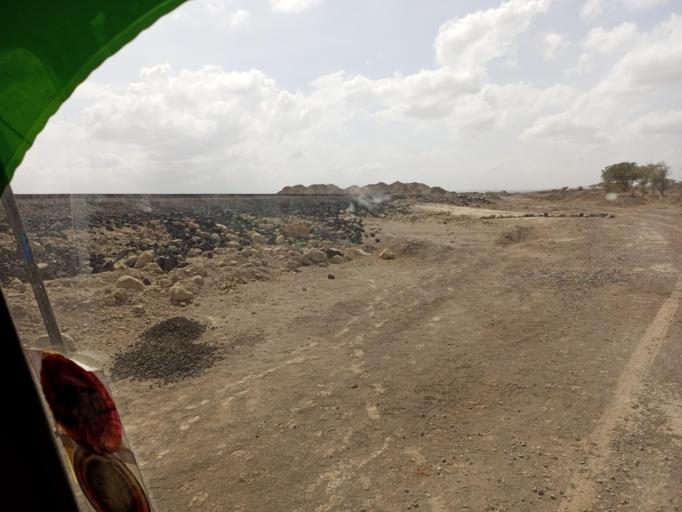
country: ET
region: Oromiya
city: Shashemene
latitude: 7.5550
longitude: 38.6732
